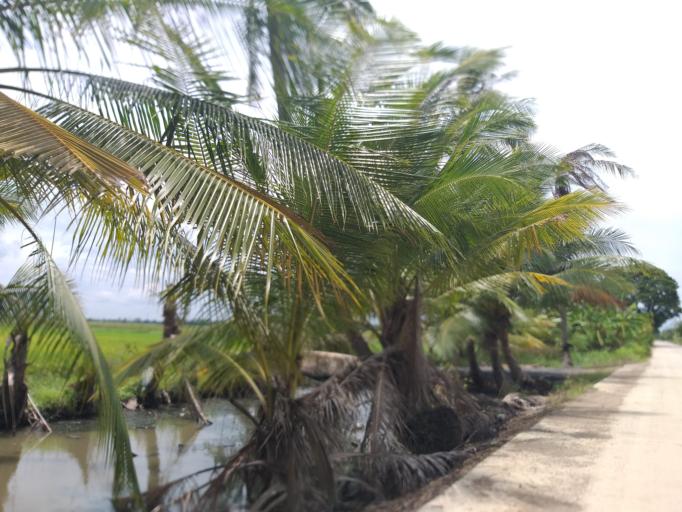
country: TH
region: Pathum Thani
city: Ban Lam Luk Ka
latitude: 14.0239
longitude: 100.8656
